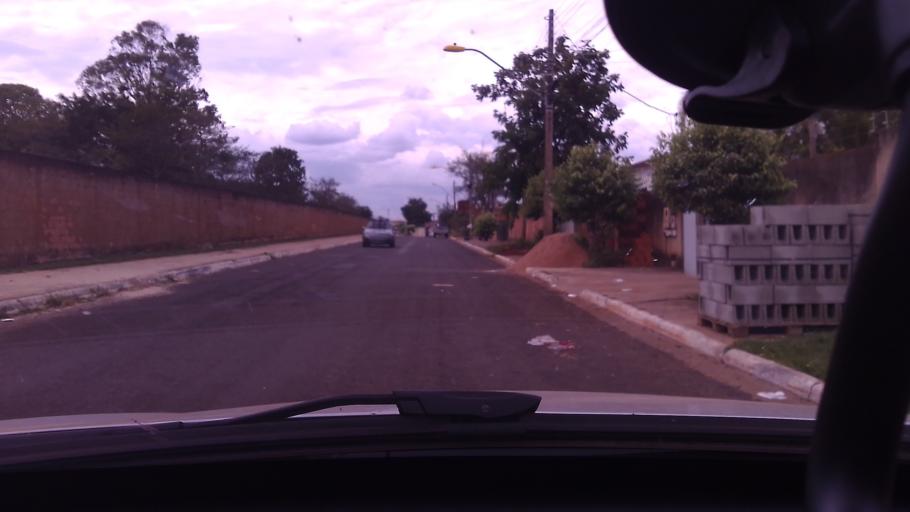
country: BR
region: Goias
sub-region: Mineiros
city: Mineiros
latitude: -17.5686
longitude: -52.5684
